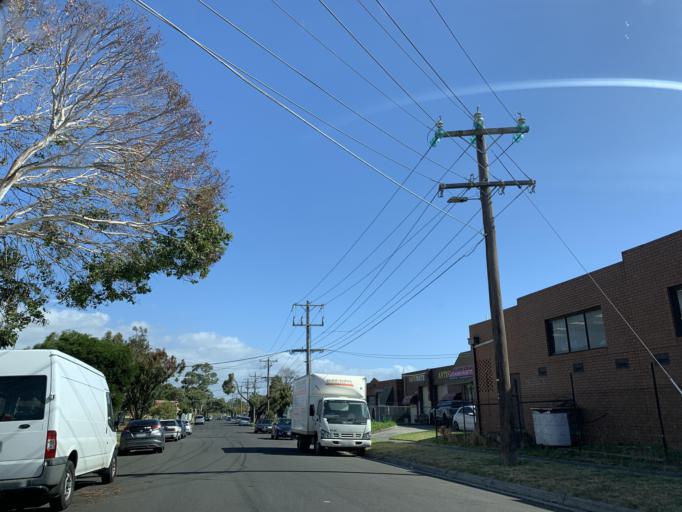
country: AU
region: Victoria
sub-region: Greater Dandenong
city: Keysborough
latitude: -37.9962
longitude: 145.1870
